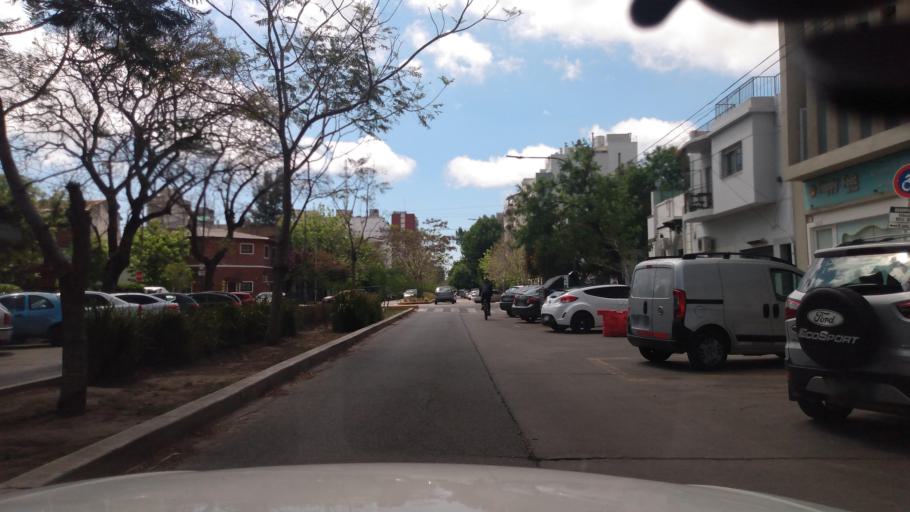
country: AR
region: Buenos Aires
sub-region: Partido de General San Martin
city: General San Martin
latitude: -34.5770
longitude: -58.4932
